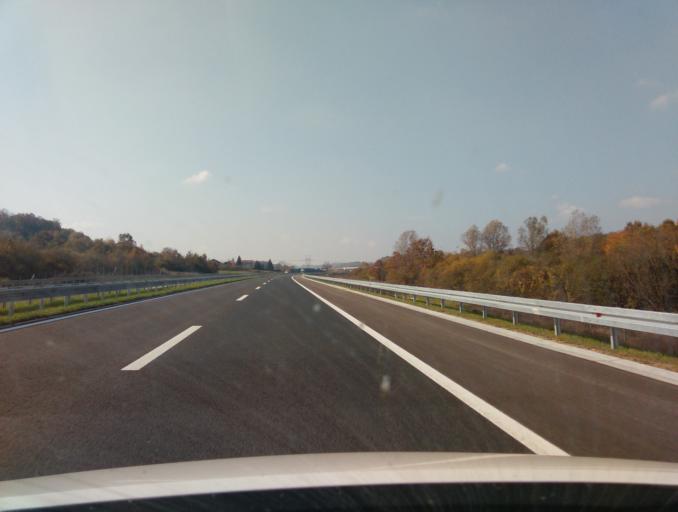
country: BA
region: Republika Srpska
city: Prnjavor
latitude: 44.8915
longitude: 17.5831
